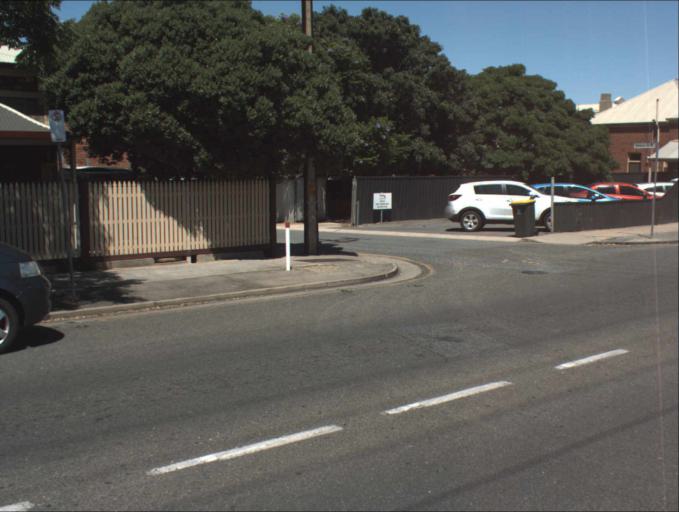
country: AU
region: South Australia
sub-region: Port Adelaide Enfield
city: Birkenhead
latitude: -34.8381
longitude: 138.4842
